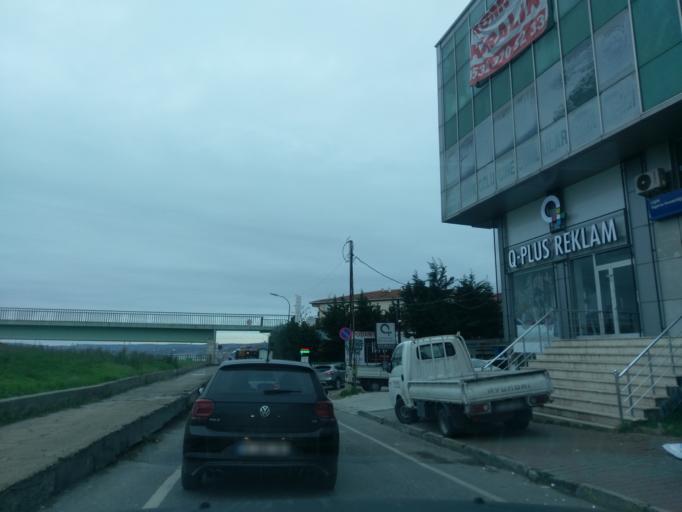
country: TR
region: Istanbul
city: Umraniye
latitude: 41.0952
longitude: 29.0969
